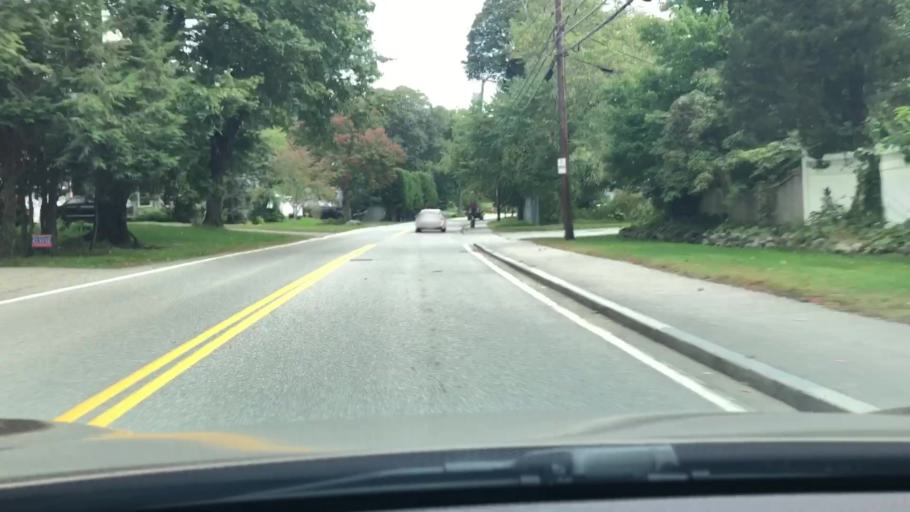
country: US
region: Massachusetts
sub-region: Middlesex County
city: Arlington
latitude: 42.4434
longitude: -71.1706
